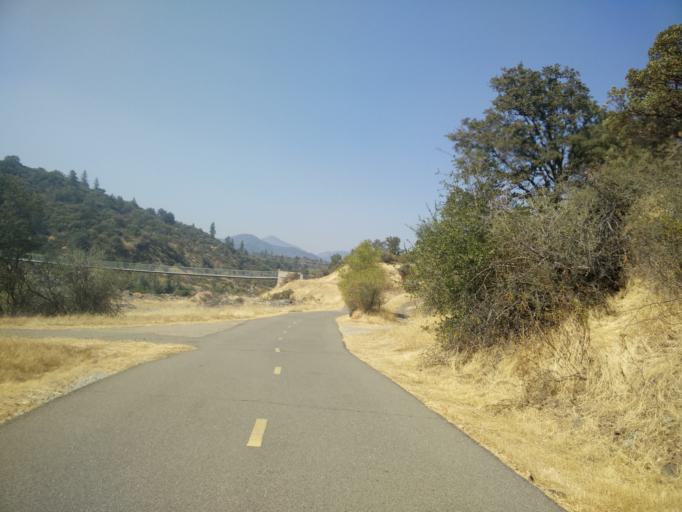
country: US
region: California
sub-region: Shasta County
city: Shasta
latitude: 40.6008
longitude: -122.4425
